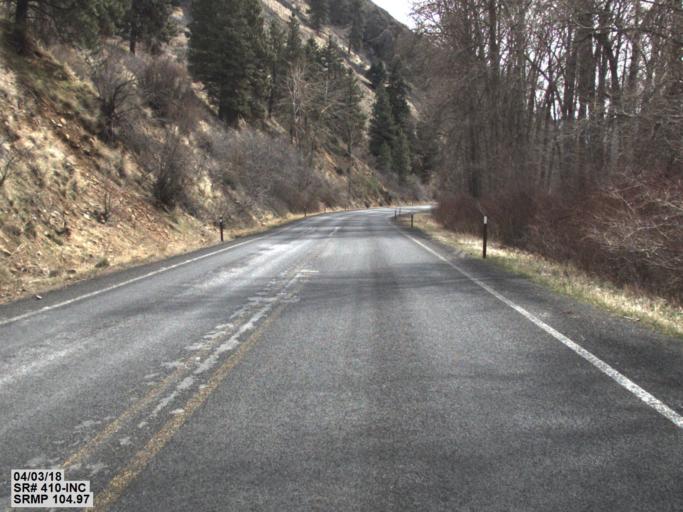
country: US
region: Washington
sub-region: Yakima County
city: Tieton
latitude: 46.8513
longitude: -120.9512
